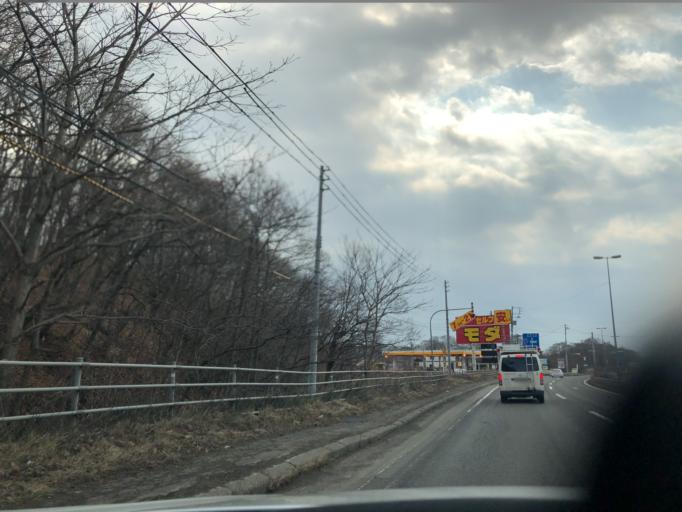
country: JP
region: Hokkaido
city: Chitose
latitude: 42.7688
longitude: 141.7088
